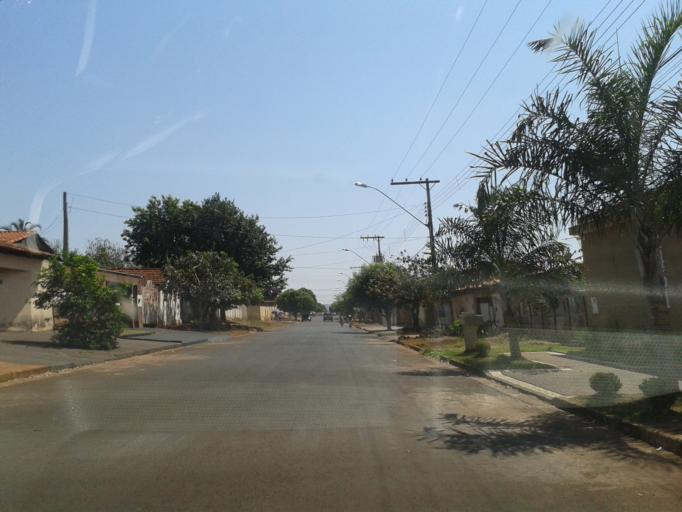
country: BR
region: Minas Gerais
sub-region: Ituiutaba
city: Ituiutaba
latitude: -18.9915
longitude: -49.4454
